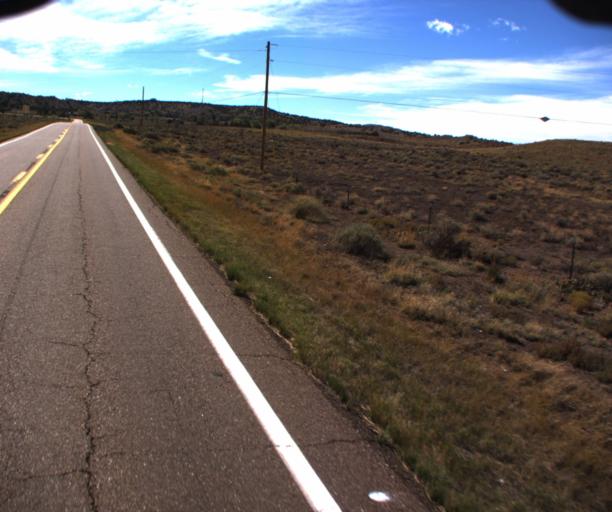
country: US
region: Arizona
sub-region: Apache County
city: Saint Johns
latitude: 34.4716
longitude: -109.6098
